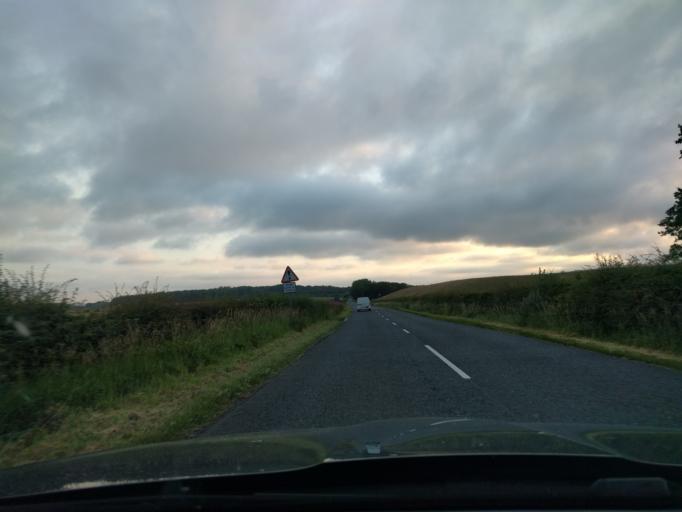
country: GB
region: England
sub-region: Northumberland
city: Stannington
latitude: 55.0850
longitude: -1.6325
